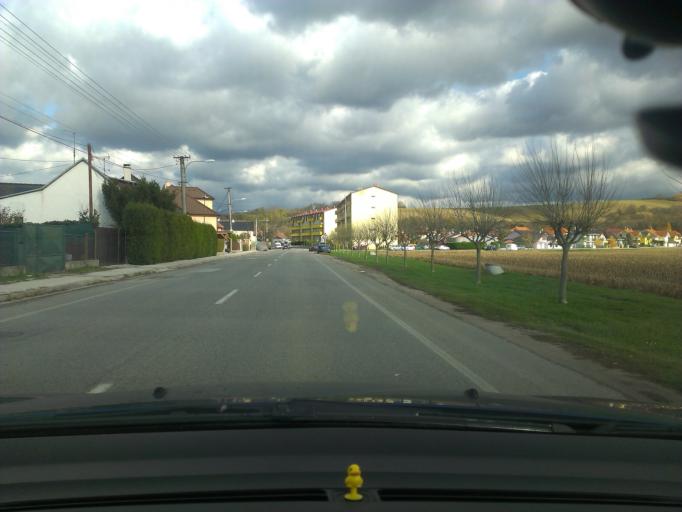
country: SK
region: Trnavsky
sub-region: Okres Trnava
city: Piestany
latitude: 48.5948
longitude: 17.8600
